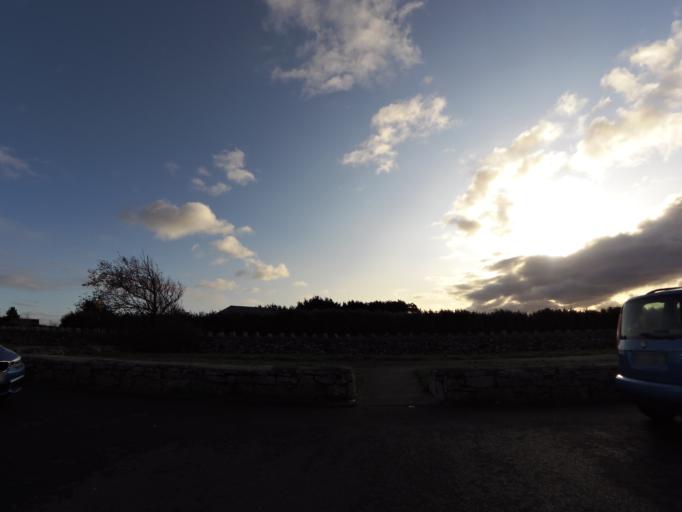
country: IE
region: Connaught
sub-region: County Galway
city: Oranmore
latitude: 53.2460
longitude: -8.9563
